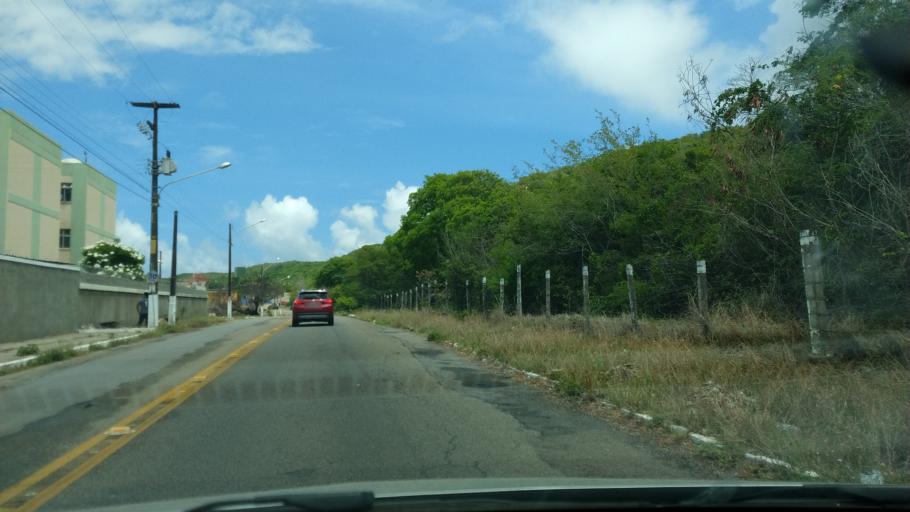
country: BR
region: Rio Grande do Norte
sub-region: Natal
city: Natal
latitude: -5.8458
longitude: -35.1965
